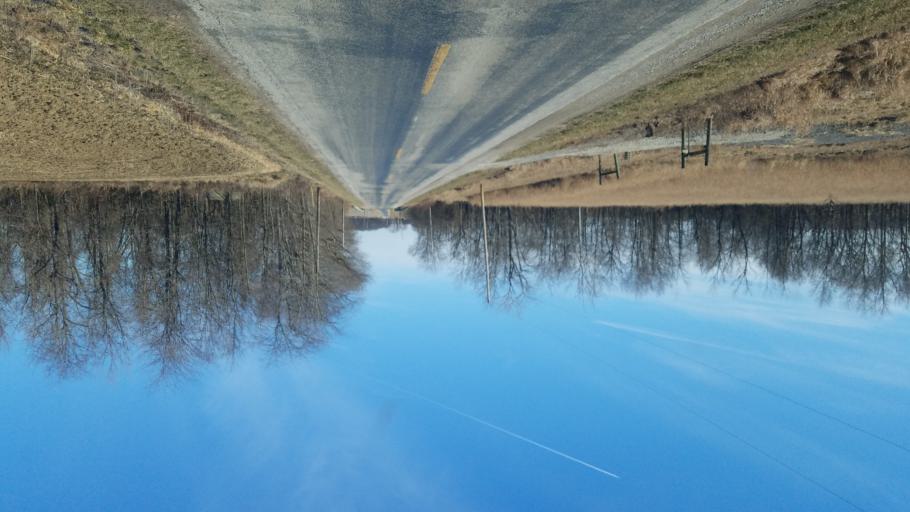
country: US
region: Ohio
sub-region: Union County
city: Richwood
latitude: 40.5251
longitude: -83.3391
